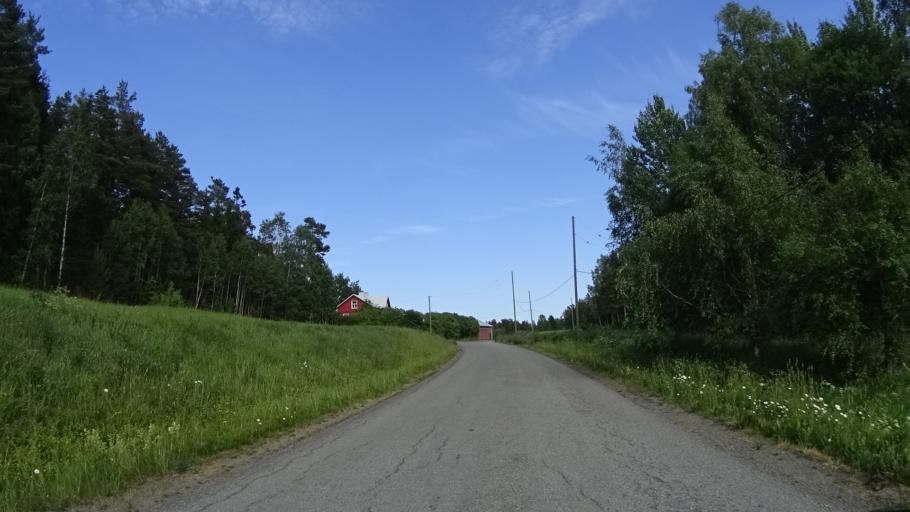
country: FI
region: Uusimaa
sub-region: Raaseporin
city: Inga
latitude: 60.0612
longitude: 23.9574
